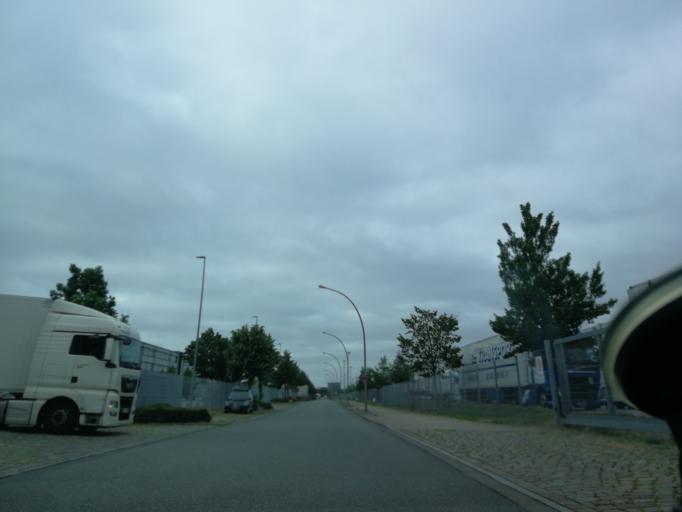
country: DE
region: Hamburg
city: Altona
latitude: 53.5065
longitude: 9.9216
